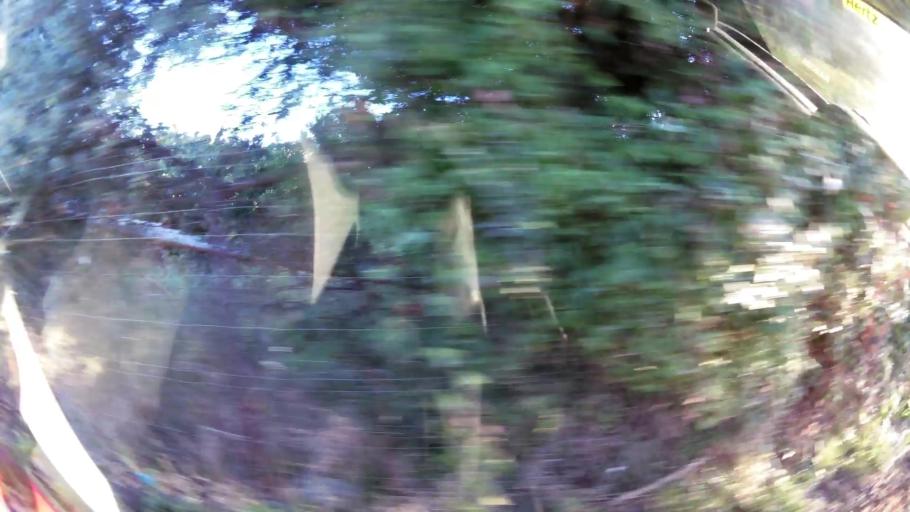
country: GR
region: Attica
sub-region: Nomarchia Anatolikis Attikis
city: Pallini
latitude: 38.0052
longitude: 23.8631
